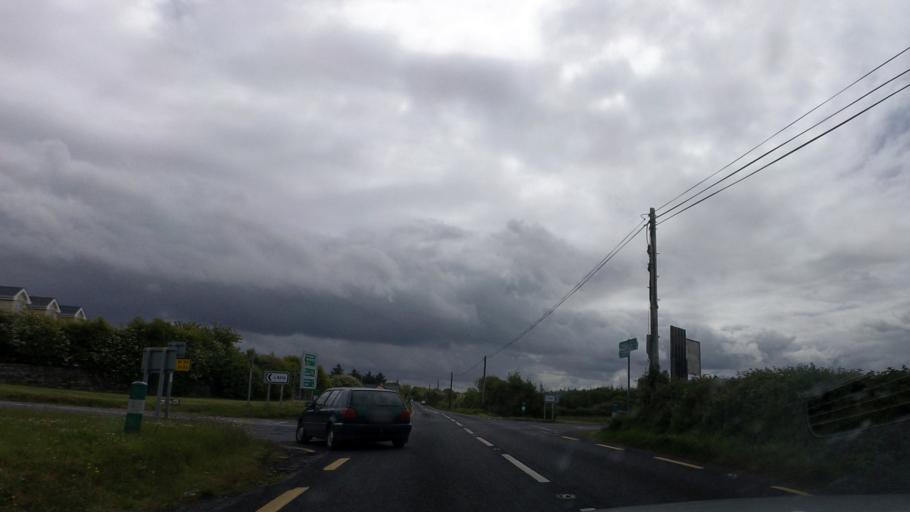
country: IE
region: Munster
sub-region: An Clar
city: Ennis
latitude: 52.9101
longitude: -9.2318
